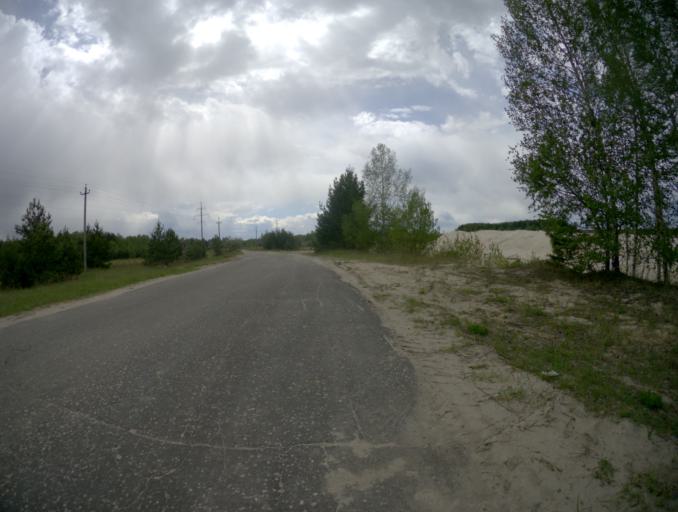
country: RU
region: Vladimir
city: Velikodvorskiy
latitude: 55.2299
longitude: 40.6495
